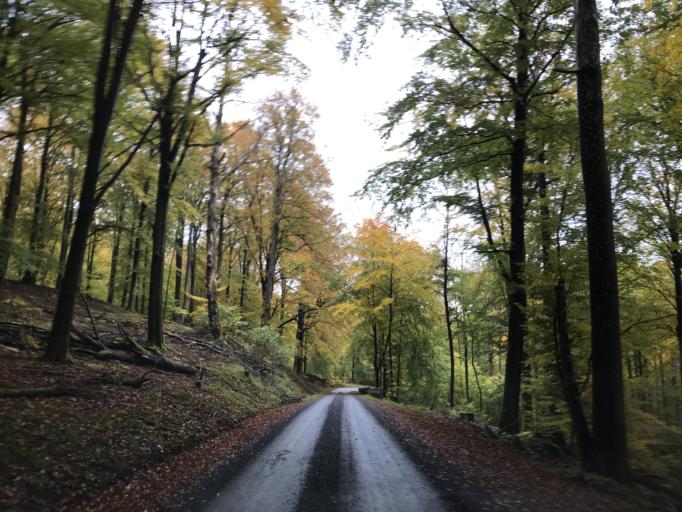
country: SE
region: Skane
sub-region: Klippans Kommun
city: Ljungbyhed
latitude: 56.0311
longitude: 13.2573
